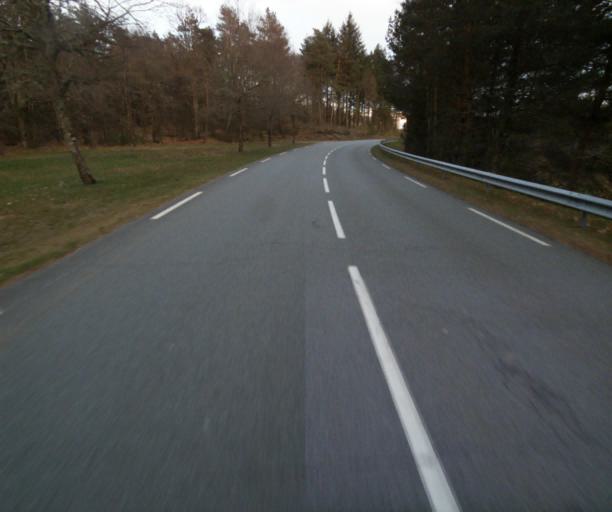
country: FR
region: Limousin
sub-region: Departement de la Correze
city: Correze
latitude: 45.2878
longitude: 1.9033
